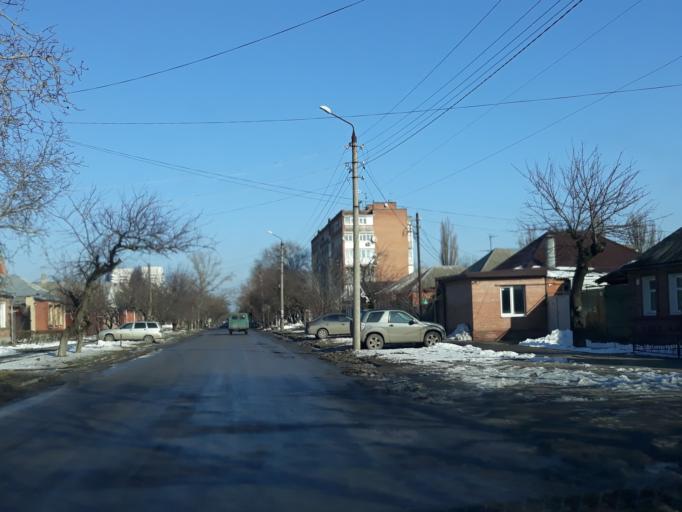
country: RU
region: Rostov
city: Taganrog
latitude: 47.2209
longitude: 38.8759
